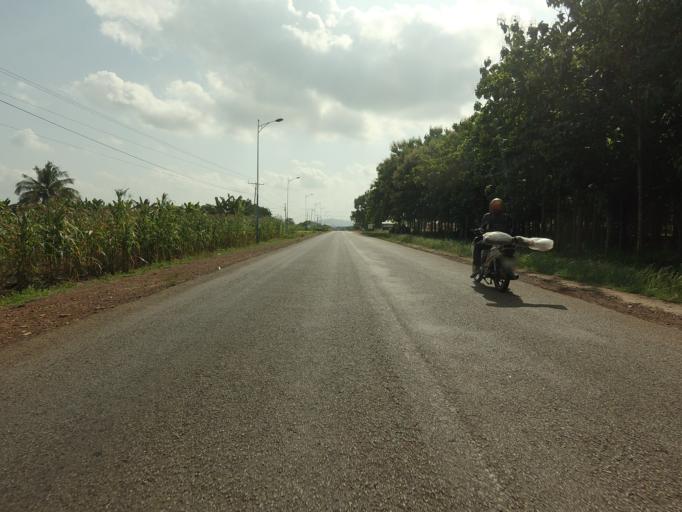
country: GH
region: Volta
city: Ho
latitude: 6.5980
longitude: 0.5171
